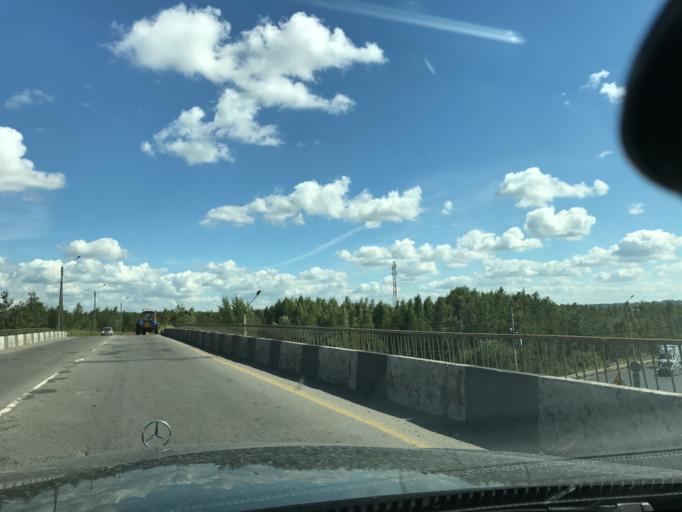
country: RU
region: Nizjnij Novgorod
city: Gorbatovka
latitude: 56.2212
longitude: 43.7494
